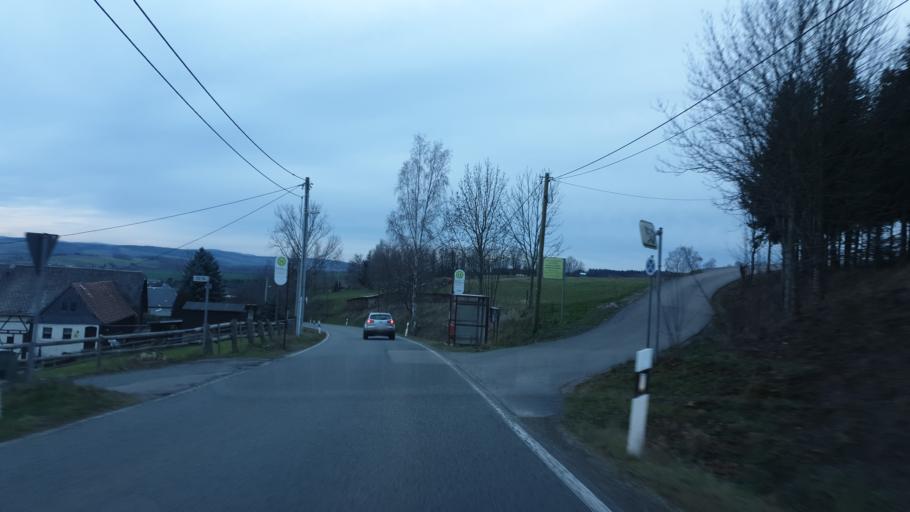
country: DE
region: Saxony
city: Hartenstein
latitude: 50.6974
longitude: 12.6779
